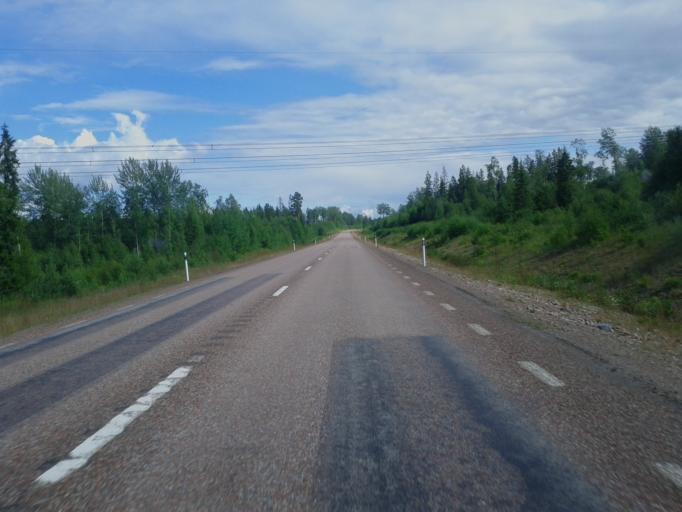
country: SE
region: Dalarna
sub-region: Rattviks Kommun
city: Raettvik
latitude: 60.8371
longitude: 15.2226
